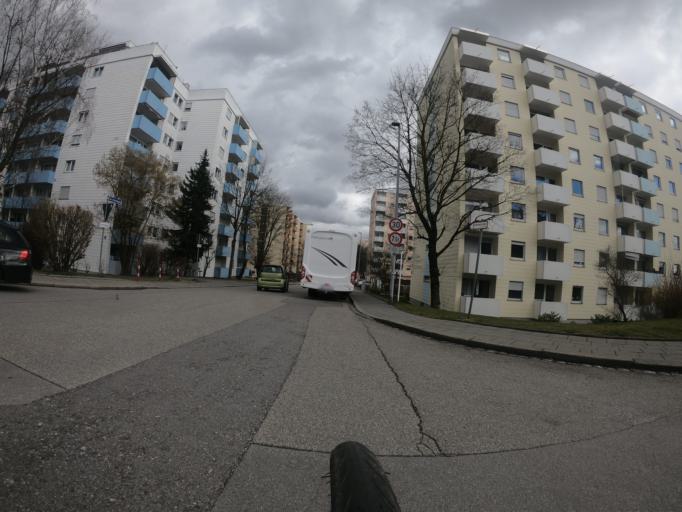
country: DE
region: Bavaria
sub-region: Upper Bavaria
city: Fuerstenfeldbruck
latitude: 48.1637
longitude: 11.2274
